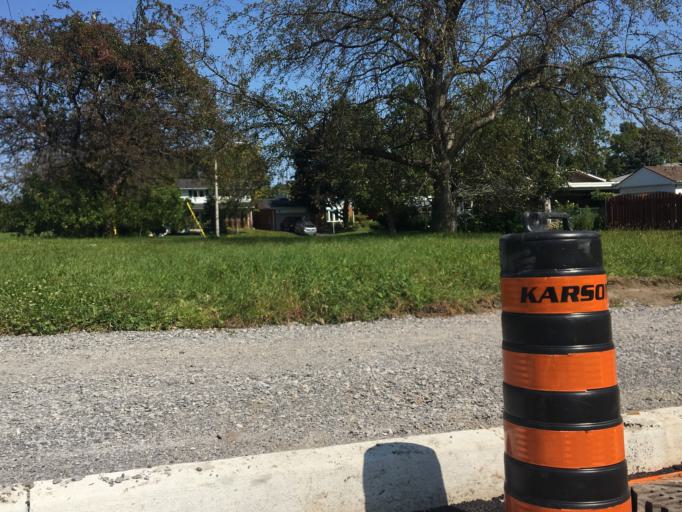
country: CA
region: Ontario
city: Ottawa
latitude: 45.3835
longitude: -75.6390
